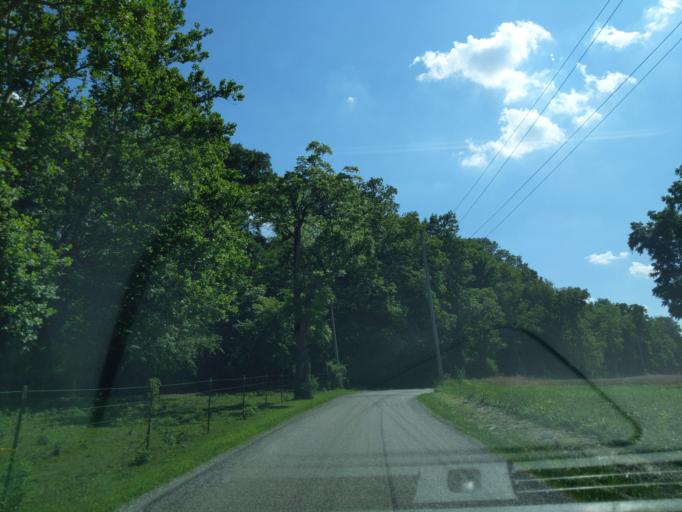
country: US
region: Indiana
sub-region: Ripley County
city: Osgood
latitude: 39.1901
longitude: -85.4020
